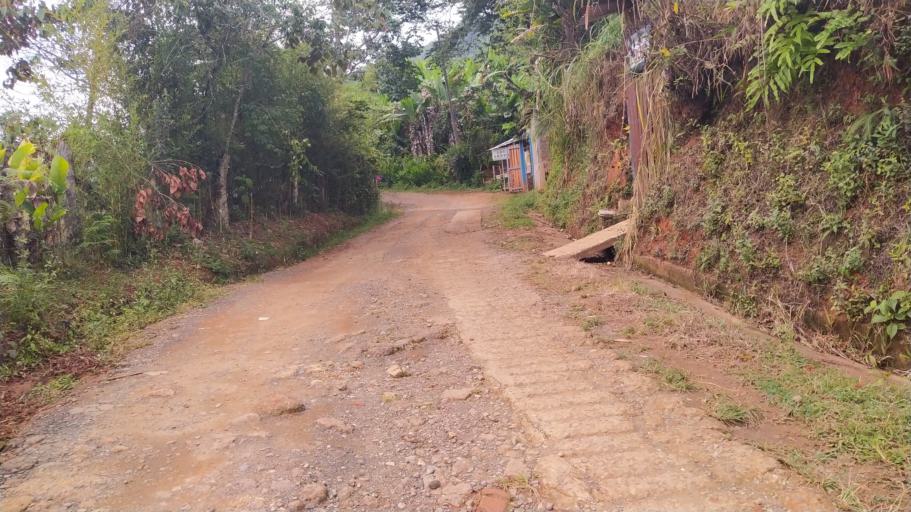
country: CO
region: Valle del Cauca
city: Cali
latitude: 3.4282
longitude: -76.6167
